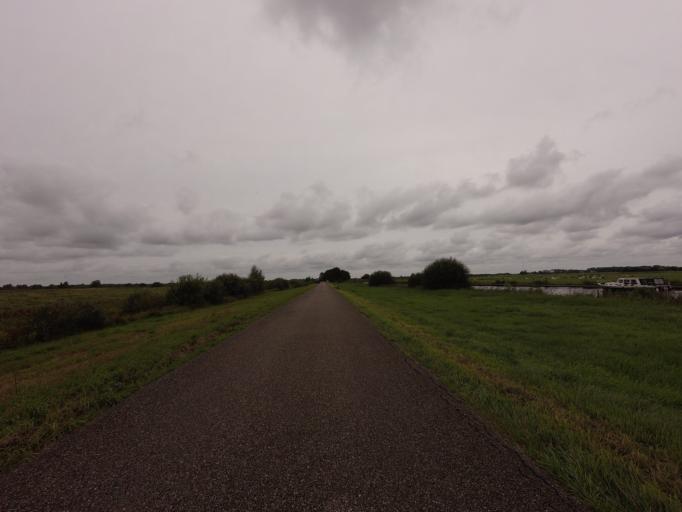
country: NL
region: Overijssel
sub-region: Gemeente Steenwijkerland
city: Oldemarkt
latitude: 52.8244
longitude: 5.9233
